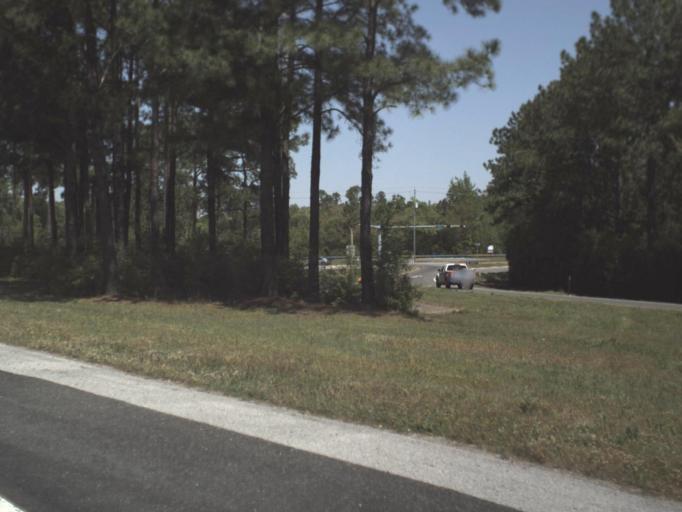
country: US
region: Florida
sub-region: Escambia County
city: Ensley
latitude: 30.5331
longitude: -87.3321
